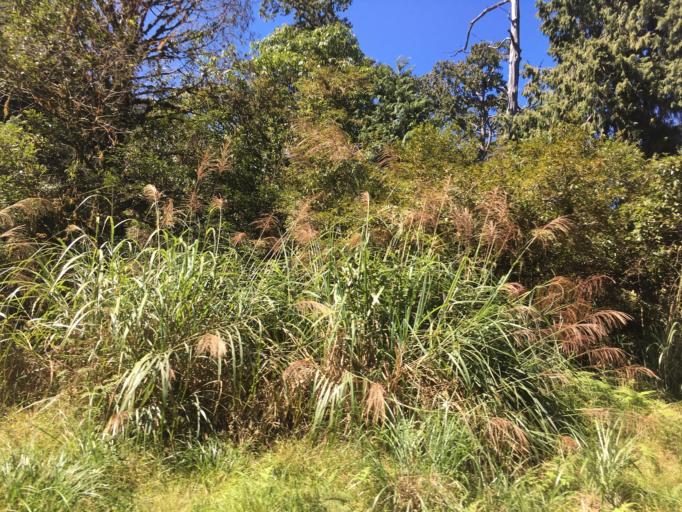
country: TW
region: Taiwan
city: Daxi
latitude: 24.5772
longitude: 121.4120
